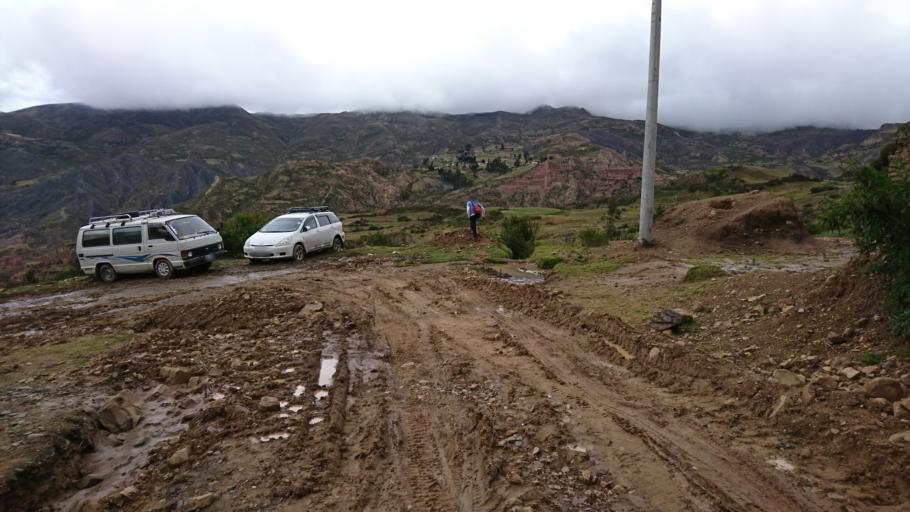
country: BO
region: La Paz
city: La Paz
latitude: -16.5472
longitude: -67.9950
